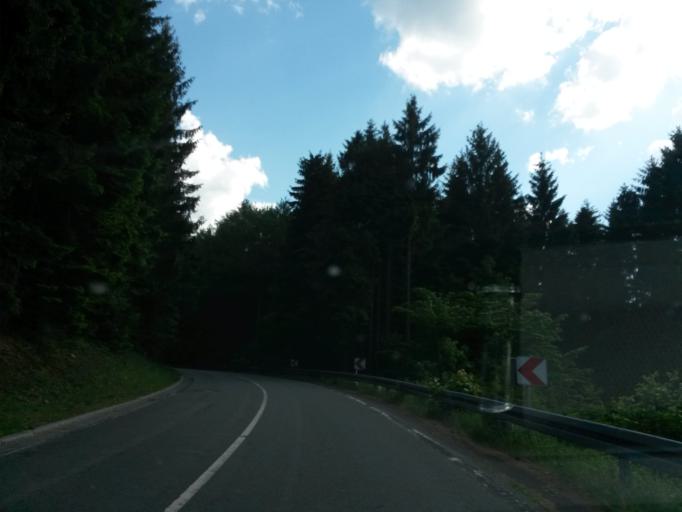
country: DE
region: North Rhine-Westphalia
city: Plettenberg
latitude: 51.2534
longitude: 7.8611
